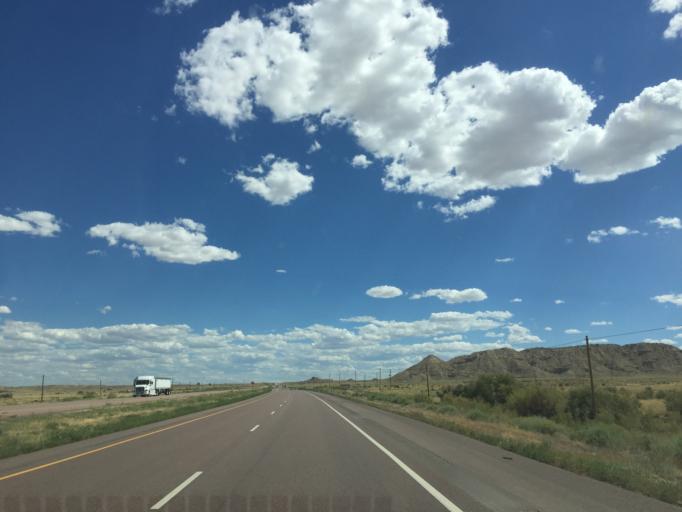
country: US
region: New Mexico
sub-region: McKinley County
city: Twin Lakes
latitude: 36.0538
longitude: -108.6788
